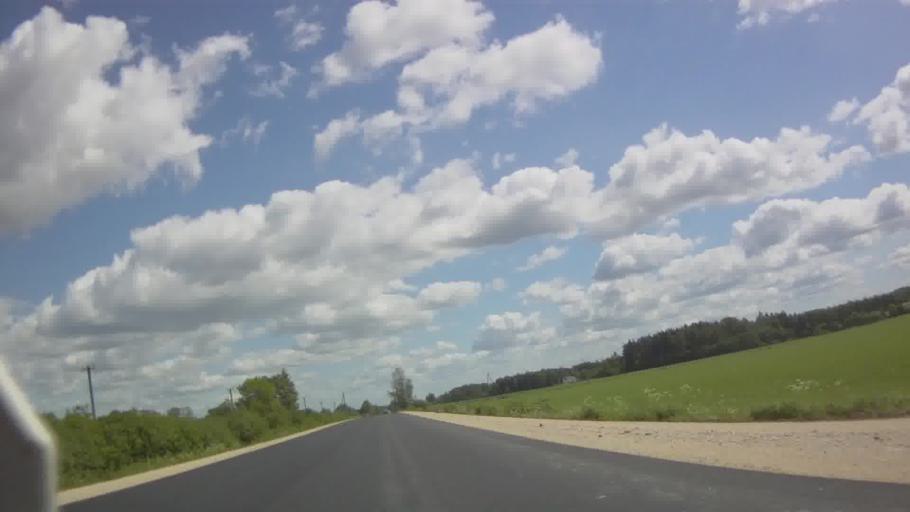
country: LV
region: Vilanu
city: Vilani
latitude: 56.5644
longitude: 26.9669
